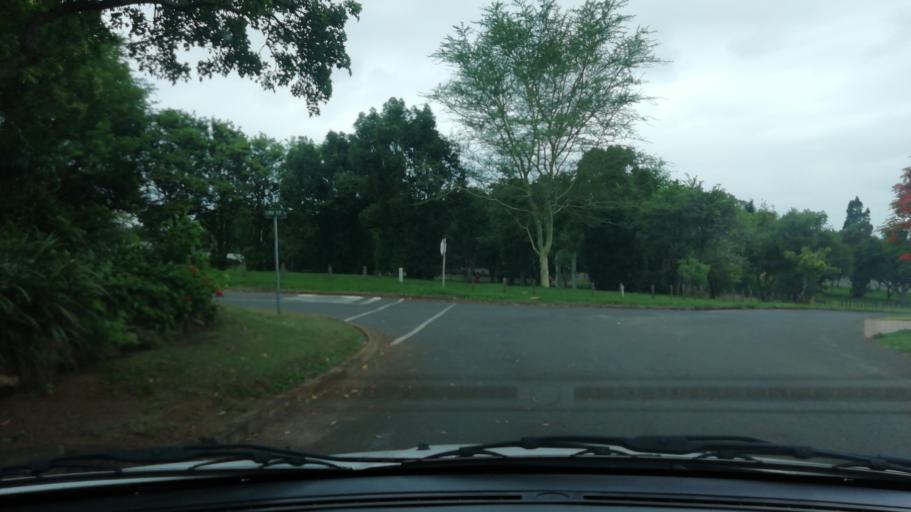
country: ZA
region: KwaZulu-Natal
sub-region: uThungulu District Municipality
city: Empangeni
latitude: -28.7639
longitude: 31.8924
